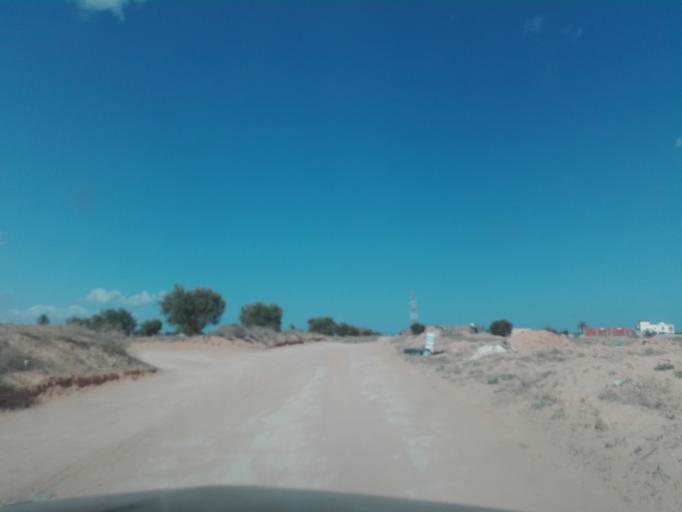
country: TN
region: Madanin
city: Bin Qirdan
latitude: 33.1644
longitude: 11.1959
